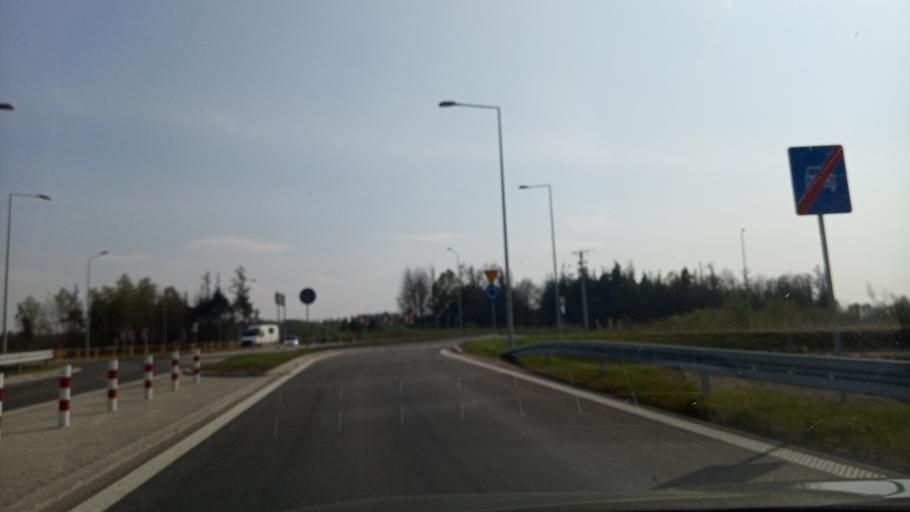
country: PL
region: West Pomeranian Voivodeship
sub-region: Powiat szczecinecki
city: Szczecinek
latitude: 53.6897
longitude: 16.7285
